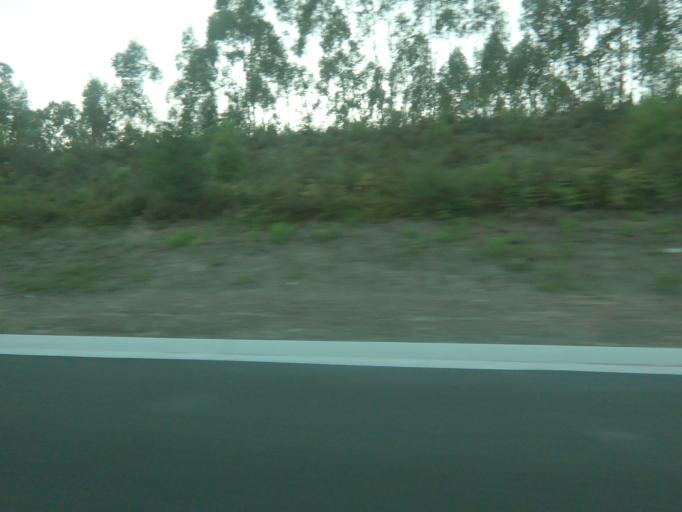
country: PT
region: Leiria
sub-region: Pombal
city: Pombal
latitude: 39.8746
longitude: -8.7020
